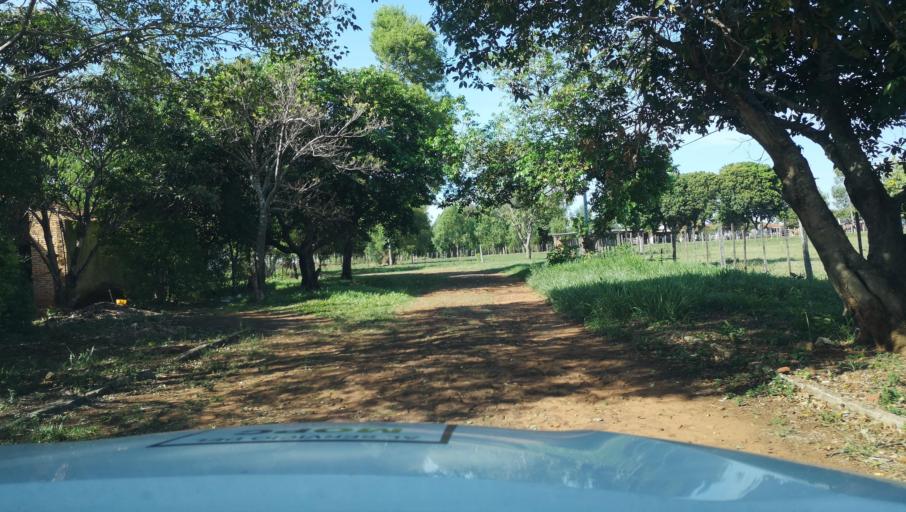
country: PY
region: Misiones
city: Santa Maria
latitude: -26.8959
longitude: -57.0184
